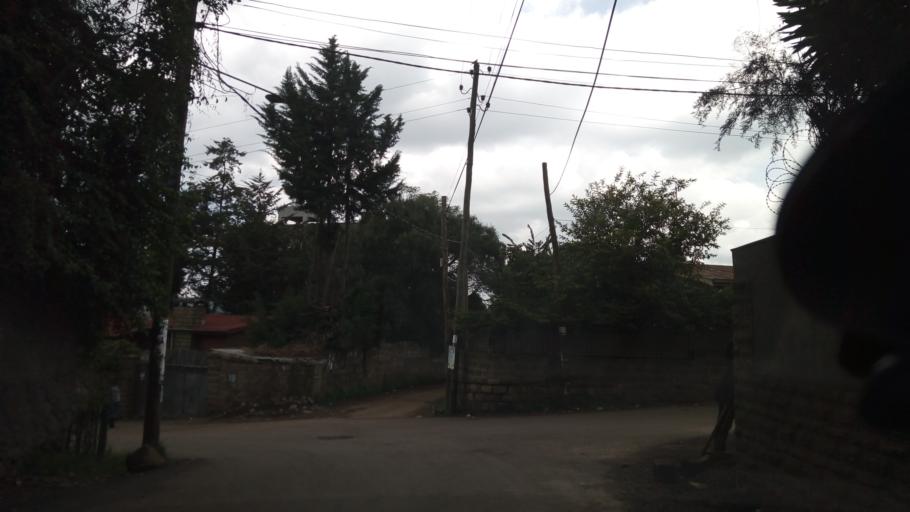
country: ET
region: Adis Abeba
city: Addis Ababa
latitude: 8.9948
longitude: 38.7154
